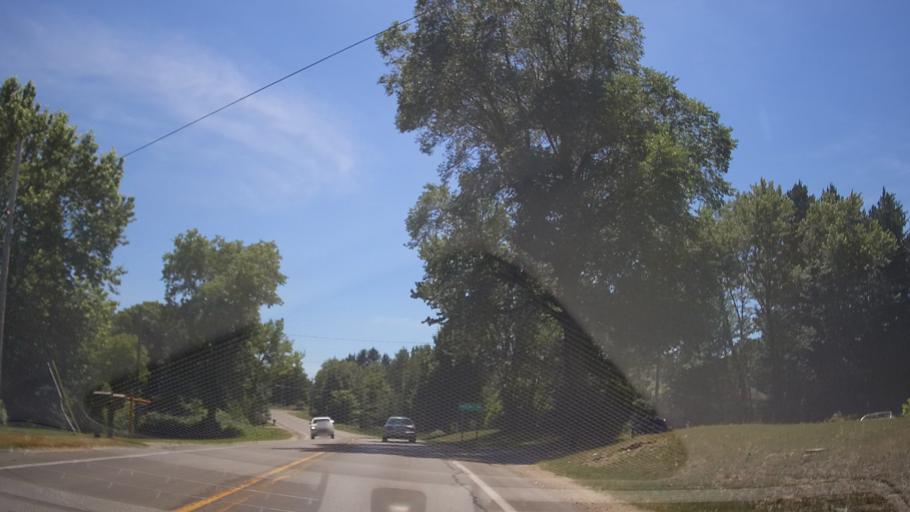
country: US
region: Michigan
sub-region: Grand Traverse County
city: Traverse City
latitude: 44.7074
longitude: -85.6925
